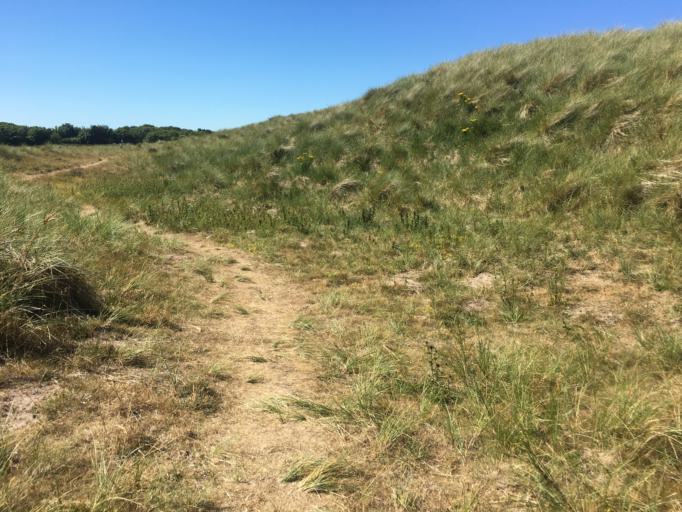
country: GB
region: England
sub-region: Northumberland
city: Beadnell
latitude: 55.5267
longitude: -1.6255
